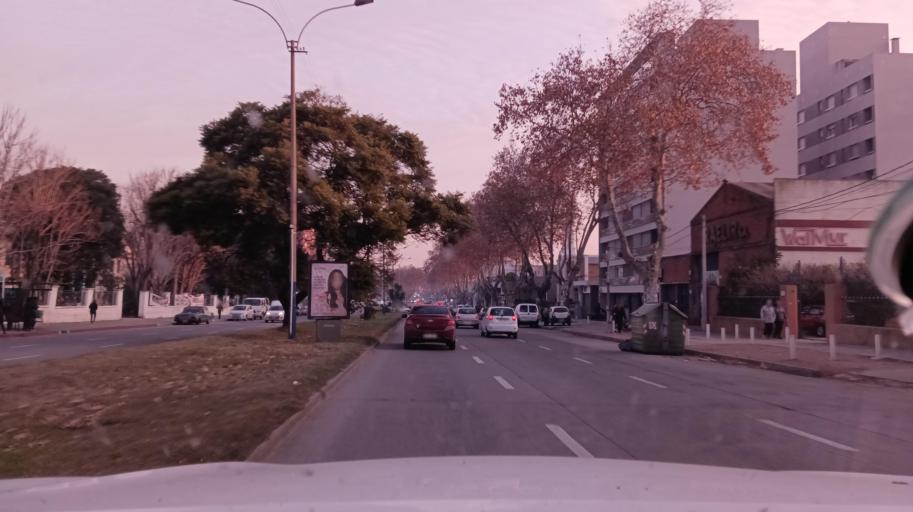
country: UY
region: Montevideo
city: Montevideo
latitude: -34.8679
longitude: -56.1726
